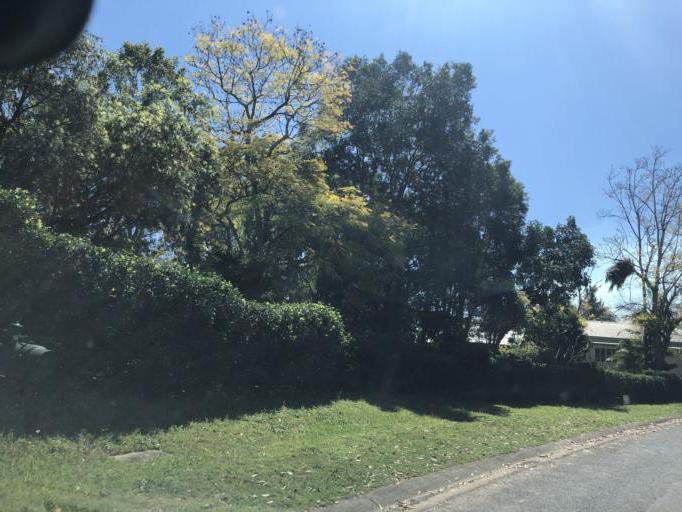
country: AU
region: New South Wales
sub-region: Bellingen
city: Bellingen
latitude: -30.4587
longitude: 152.8977
